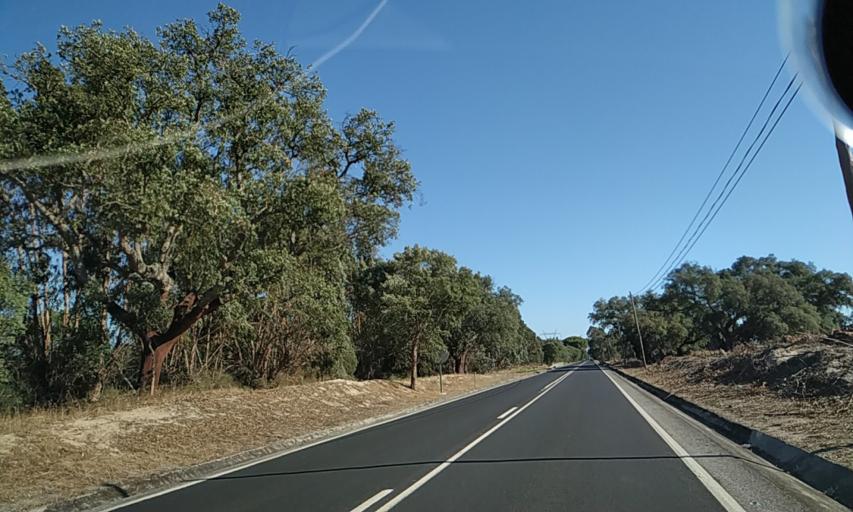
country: PT
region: Santarem
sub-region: Benavente
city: Samora Correia
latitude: 38.8582
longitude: -8.8811
